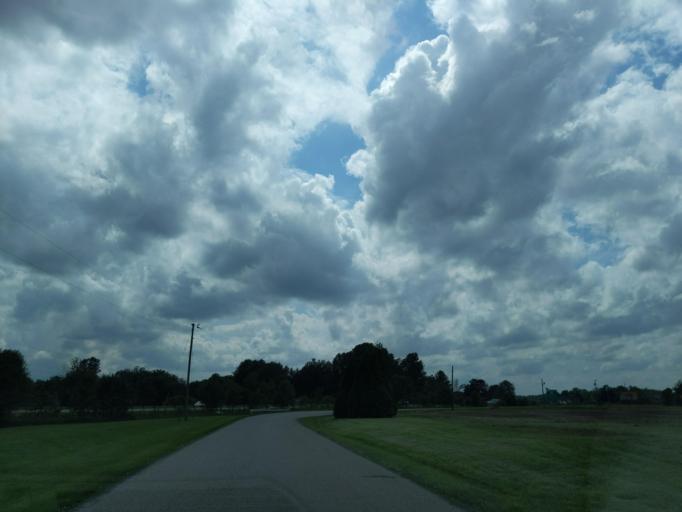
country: US
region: Indiana
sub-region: Ripley County
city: Batesville
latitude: 39.3031
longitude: -85.1992
